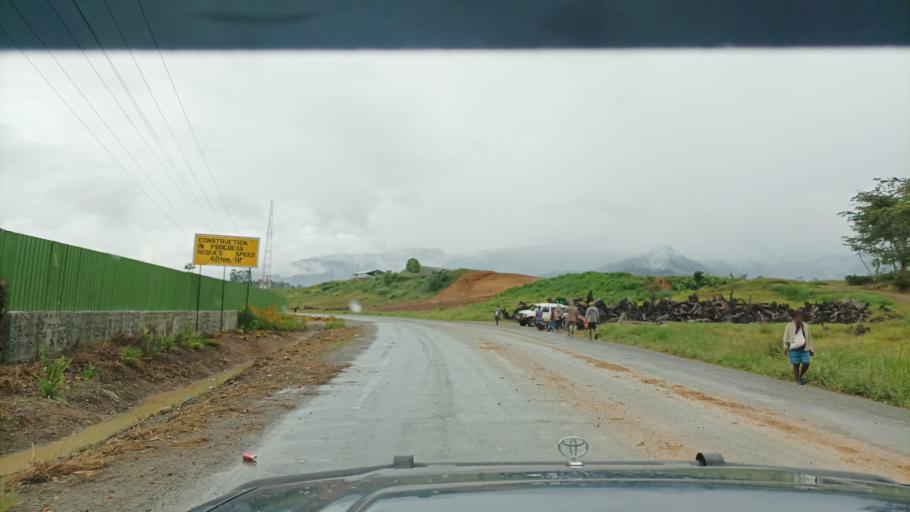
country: PG
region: Jiwaka
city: Minj
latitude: -5.8464
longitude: 144.6222
